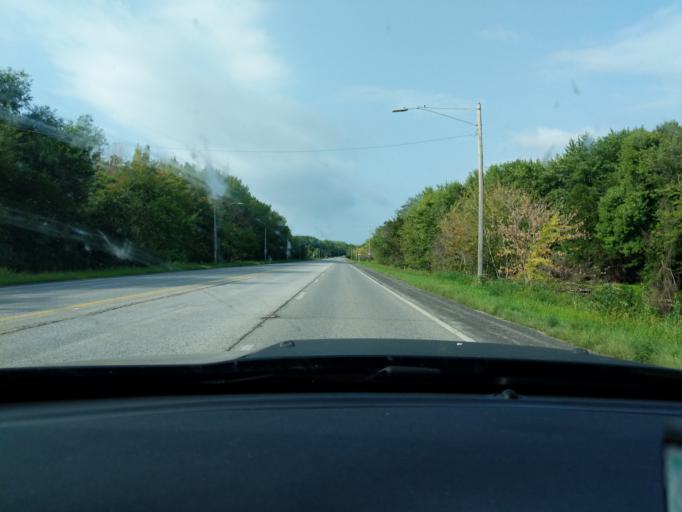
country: US
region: Illinois
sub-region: Rock Island County
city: Rock Island
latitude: 41.5066
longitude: -90.6118
